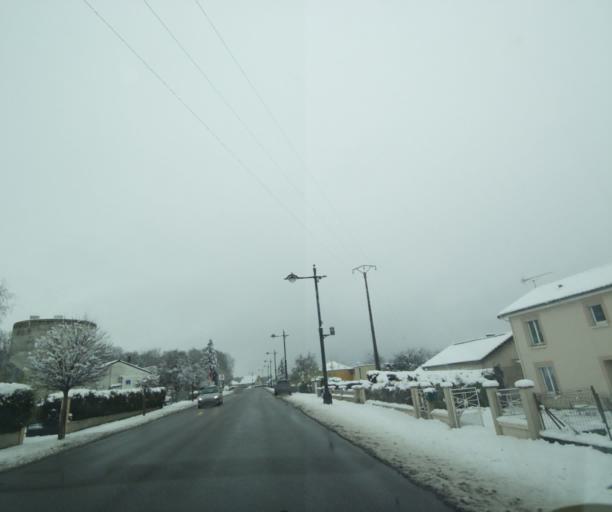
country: FR
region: Champagne-Ardenne
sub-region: Departement de la Haute-Marne
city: Montier-en-Der
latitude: 48.4833
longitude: 4.7718
